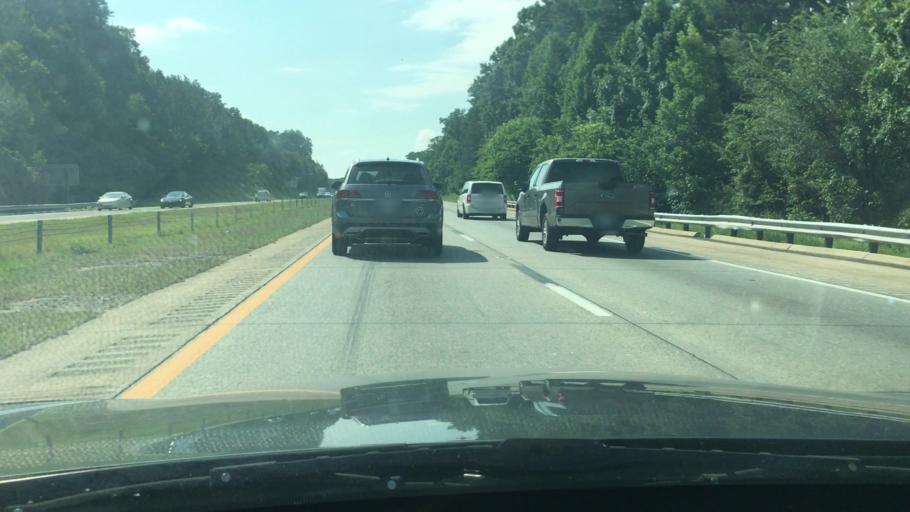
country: US
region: North Carolina
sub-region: Orange County
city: Chapel Hill
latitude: 35.9640
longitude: -79.0200
